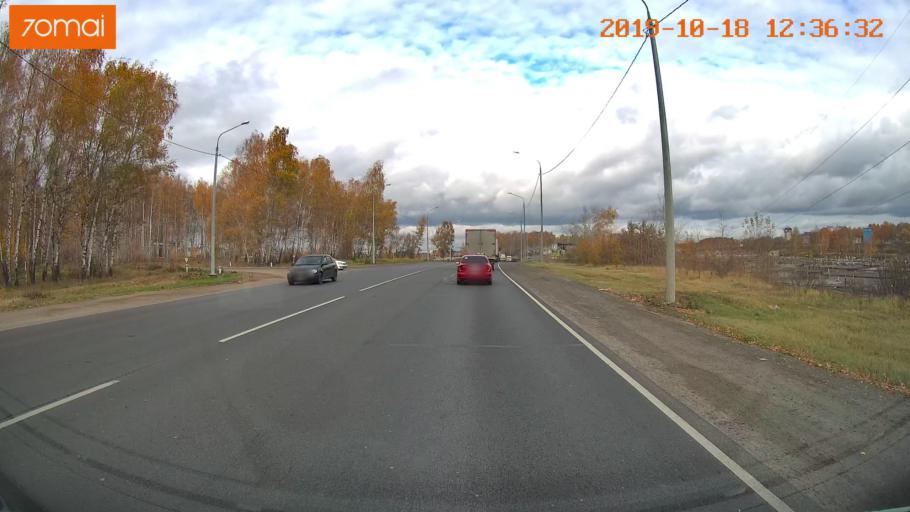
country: RU
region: Rjazan
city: Ryazan'
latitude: 54.6362
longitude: 39.6341
